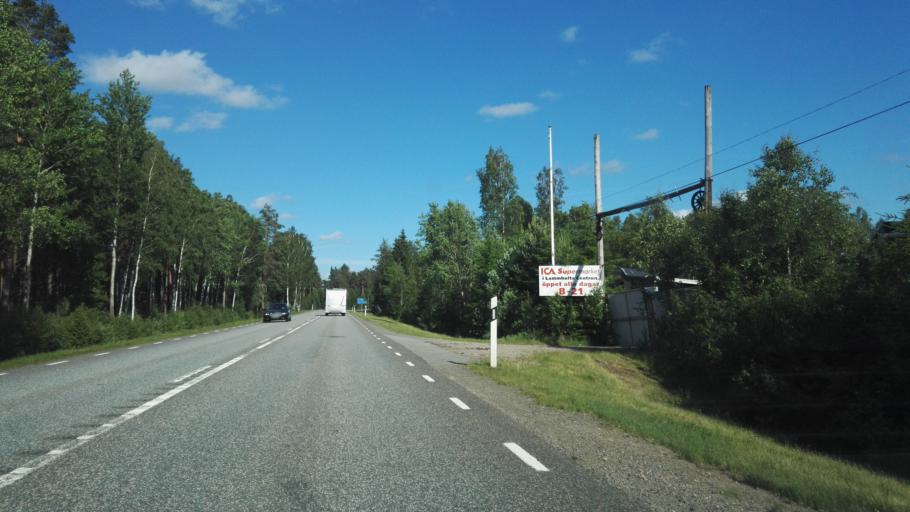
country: SE
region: Kronoberg
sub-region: Vaxjo Kommun
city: Lammhult
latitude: 57.1796
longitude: 14.5579
